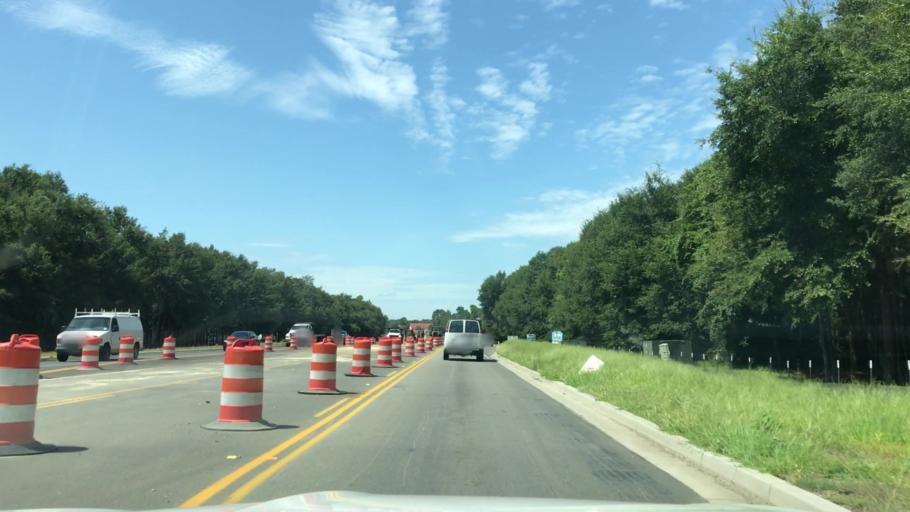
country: US
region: South Carolina
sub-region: Charleston County
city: North Charleston
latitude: 32.9050
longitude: -79.9102
